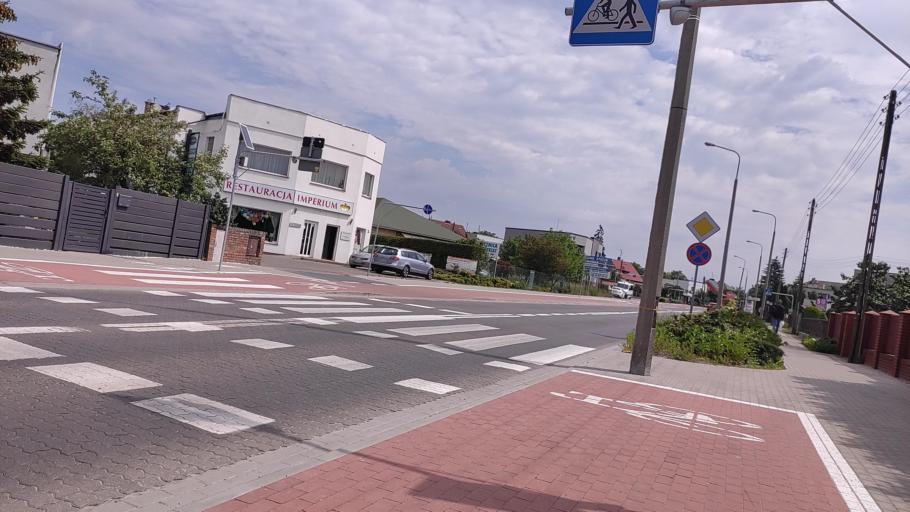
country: PL
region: Greater Poland Voivodeship
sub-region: Powiat poznanski
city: Swarzedz
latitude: 52.4022
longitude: 17.0721
